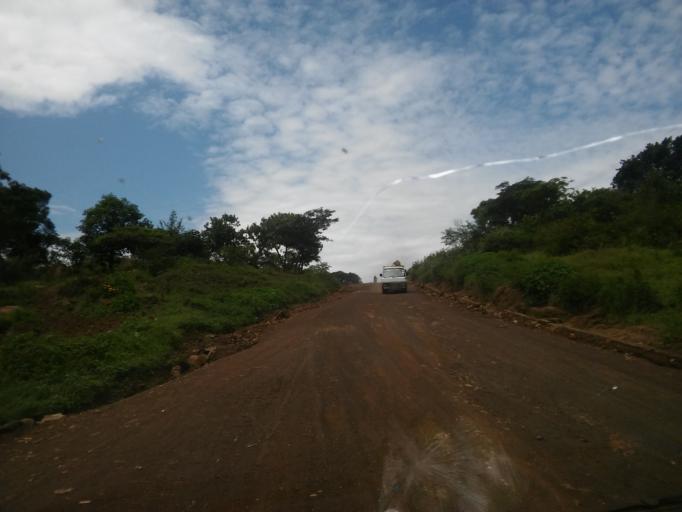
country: UG
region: Eastern Region
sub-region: Tororo District
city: Tororo
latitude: 0.8166
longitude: 34.2994
